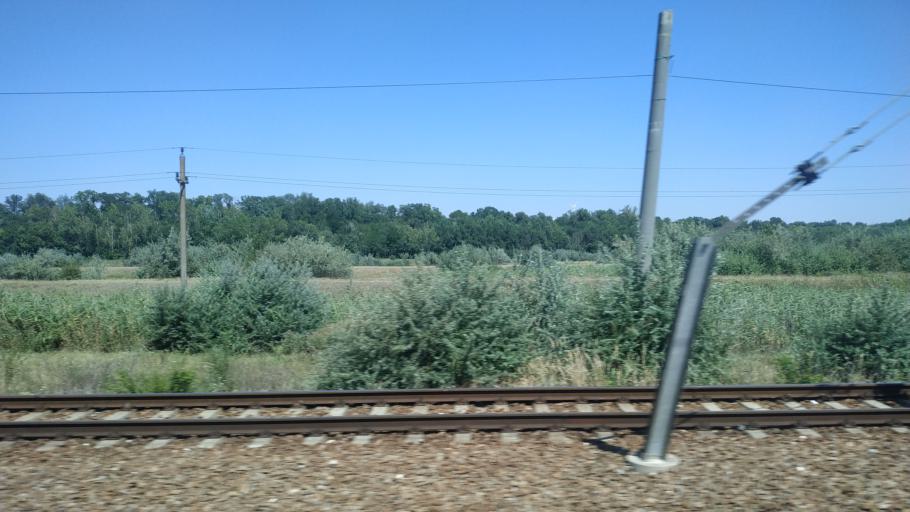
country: RO
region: Constanta
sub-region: Comuna Mircea Voda
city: Mircea Voda
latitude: 44.2654
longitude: 28.1497
